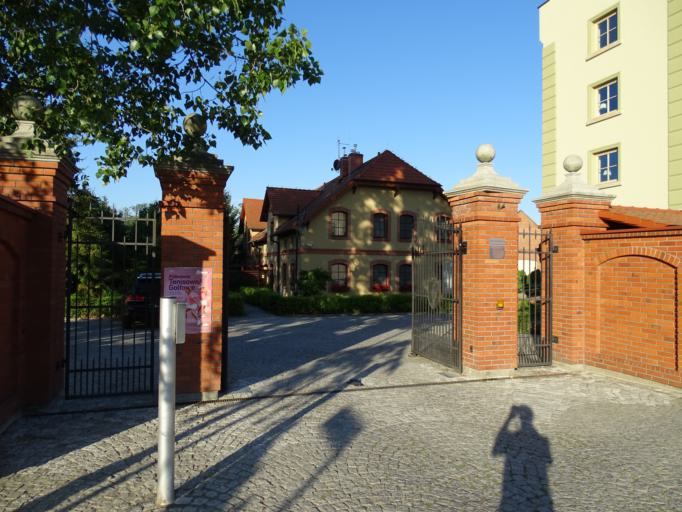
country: PL
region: Lower Silesian Voivodeship
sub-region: Powiat wroclawski
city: Bielany Wroclawskie
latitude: 51.0346
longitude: 16.9930
